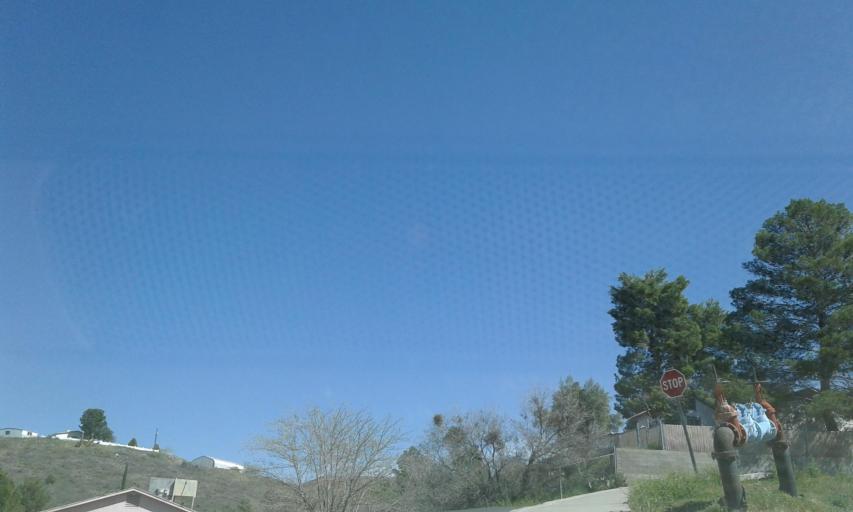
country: US
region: Arizona
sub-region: Gila County
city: Central Heights-Midland City
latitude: 33.4208
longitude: -110.8101
